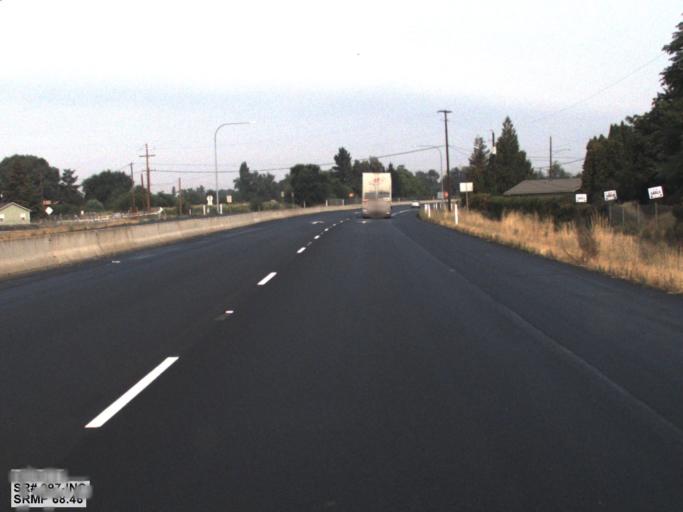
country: US
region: Washington
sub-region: Yakima County
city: Wapato
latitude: 46.4394
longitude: -120.4266
